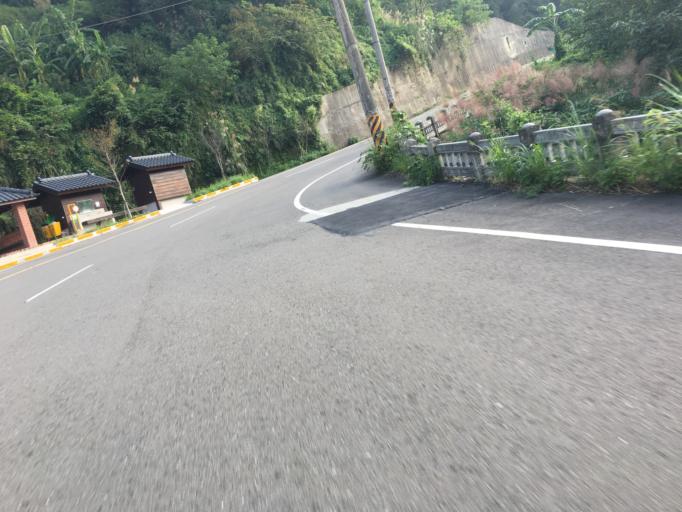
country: TW
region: Taiwan
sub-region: Hsinchu
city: Hsinchu
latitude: 24.7271
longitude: 121.0347
